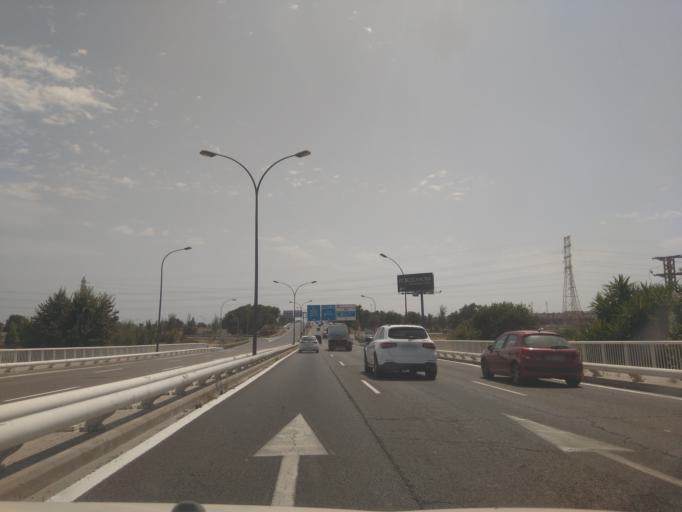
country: ES
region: Valencia
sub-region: Provincia de Valencia
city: Sedavi
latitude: 39.4399
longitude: -0.3696
